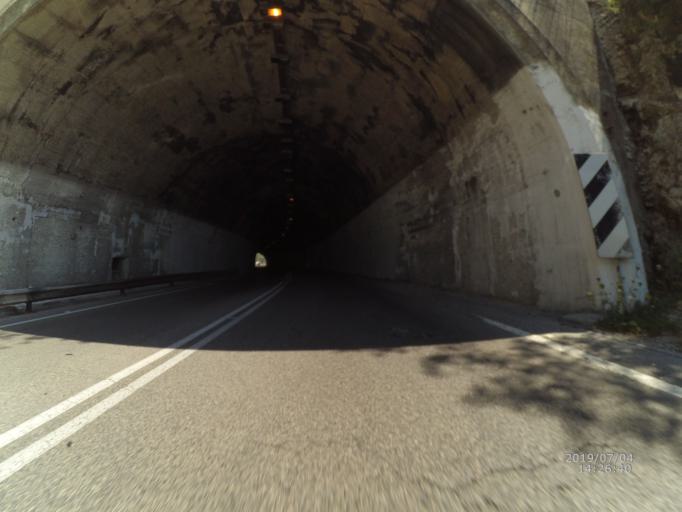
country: IT
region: Latium
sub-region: Provincia di Latina
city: Sperlonga
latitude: 41.2414
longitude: 13.4620
